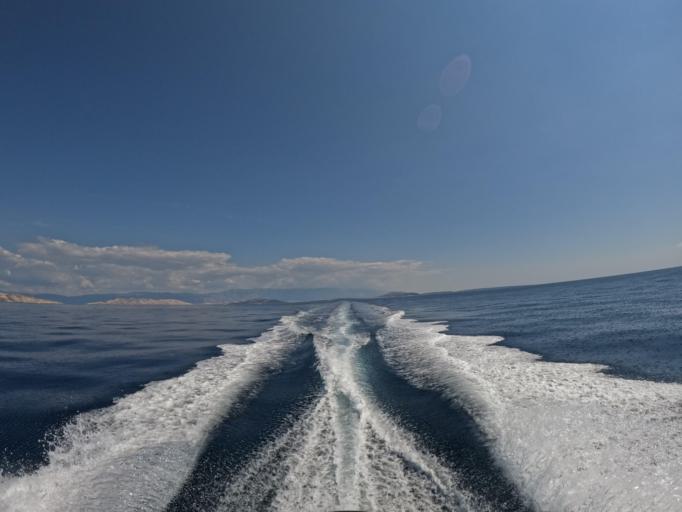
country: HR
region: Primorsko-Goranska
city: Punat
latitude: 44.9078
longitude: 14.5976
